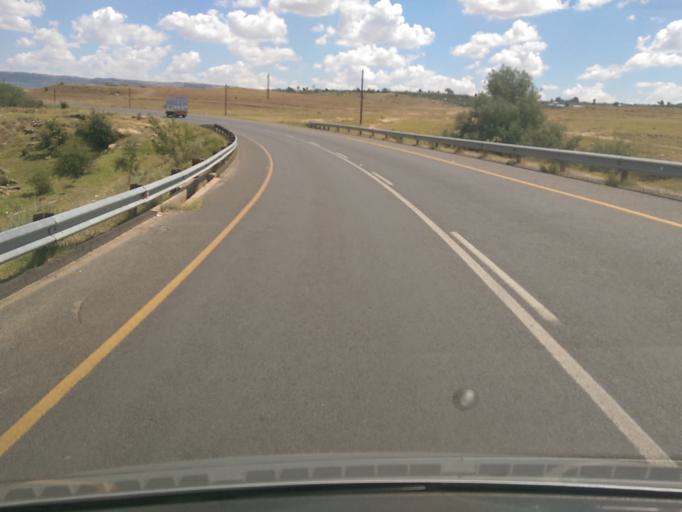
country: LS
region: Maseru
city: Maseru
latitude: -29.3903
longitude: 27.5495
